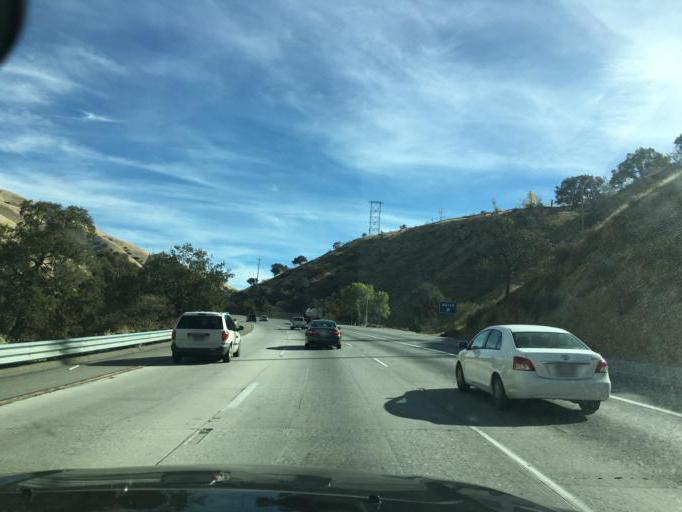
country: US
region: California
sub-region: Kern County
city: Lebec
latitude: 34.8915
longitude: -118.9158
